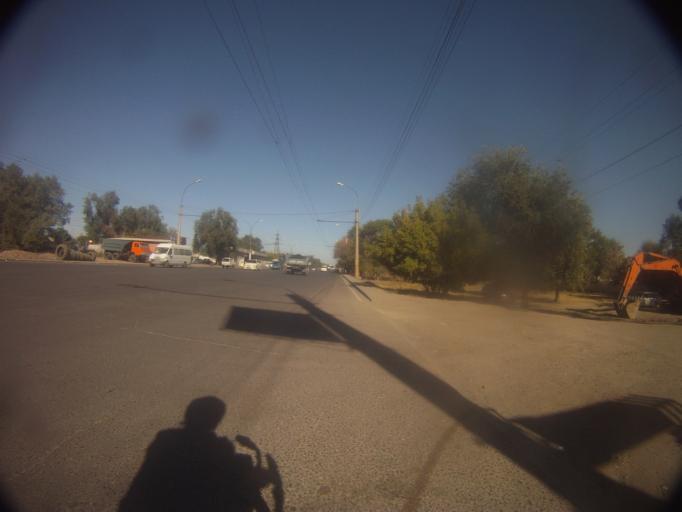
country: KG
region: Chuy
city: Bishkek
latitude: 42.8739
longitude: 74.5180
